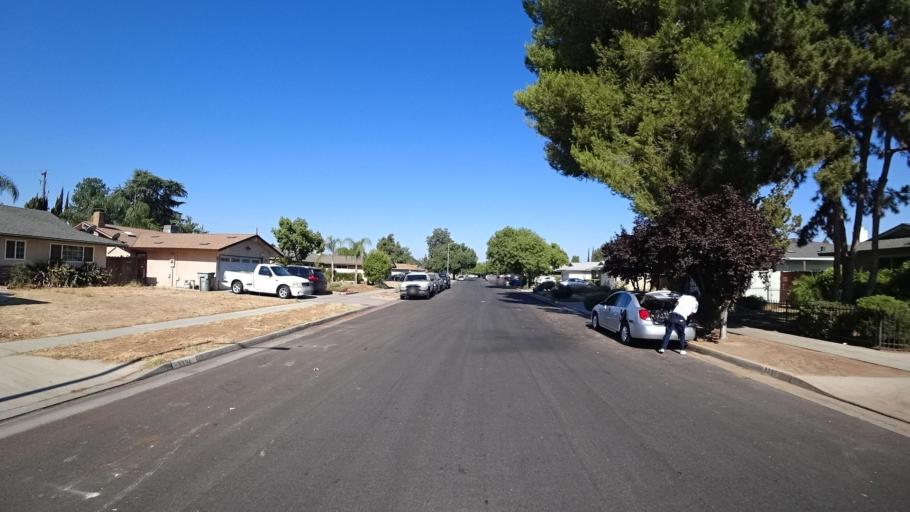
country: US
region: California
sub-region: Fresno County
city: Fresno
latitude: 36.7851
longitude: -119.7680
